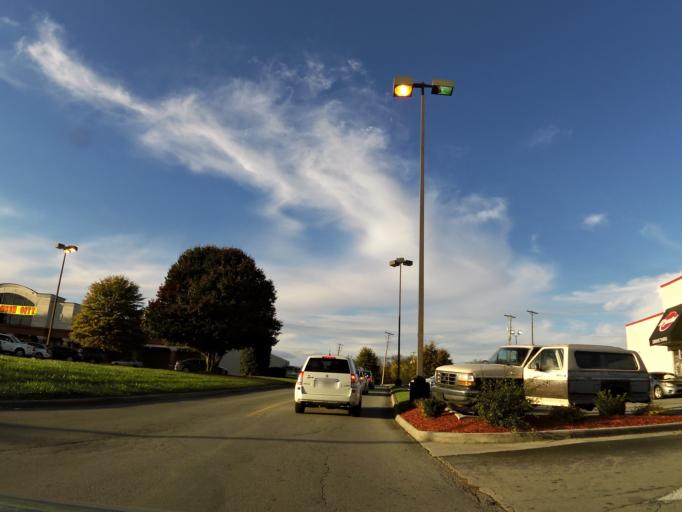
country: US
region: Tennessee
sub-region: Knox County
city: Farragut
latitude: 35.9139
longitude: -84.0797
